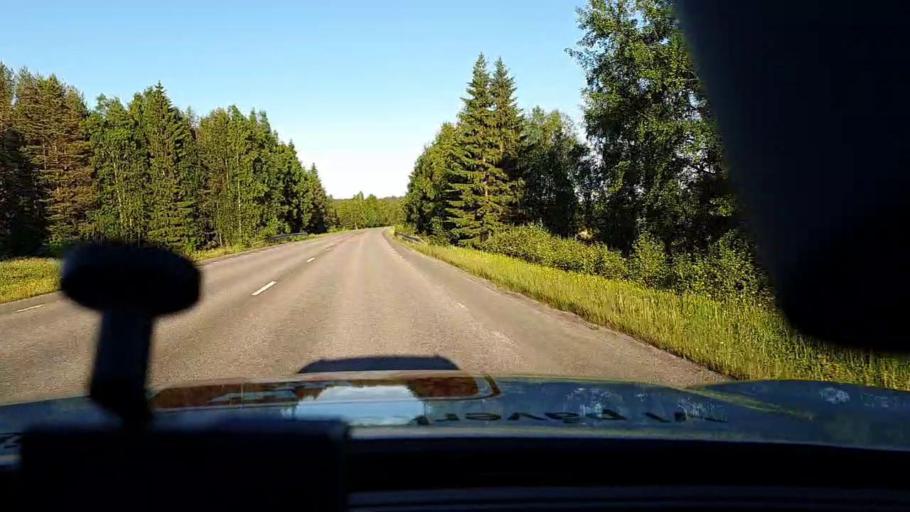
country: SE
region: Norrbotten
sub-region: Lulea Kommun
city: Lulea
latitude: 65.6140
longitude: 22.1548
